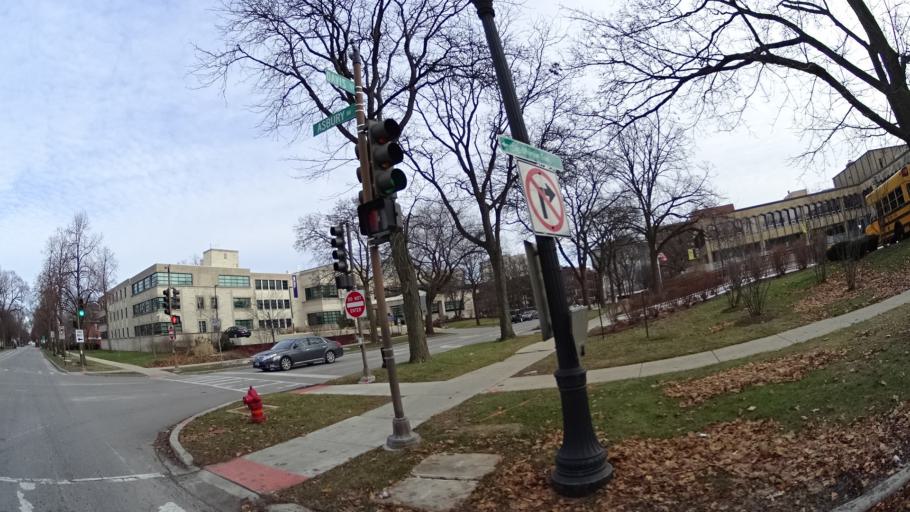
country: US
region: Illinois
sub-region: Cook County
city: Evanston
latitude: 42.0472
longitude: -87.6901
